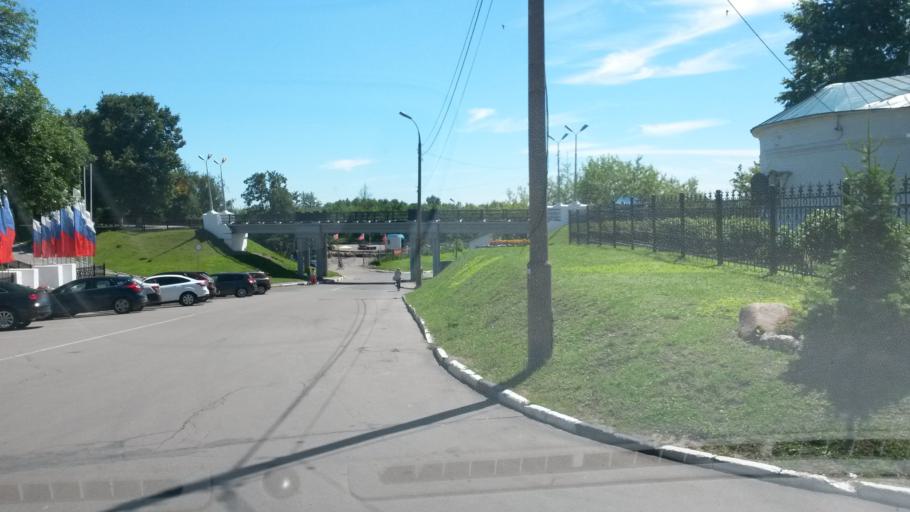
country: RU
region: Jaroslavl
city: Yaroslavl
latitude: 57.6229
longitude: 39.8960
